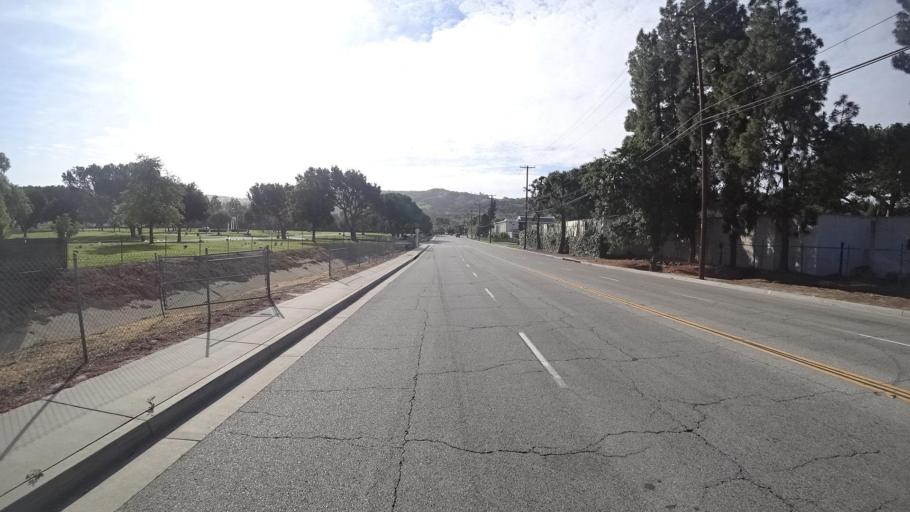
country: US
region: California
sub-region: Los Angeles County
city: South El Monte
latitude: 34.0153
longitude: -118.0488
